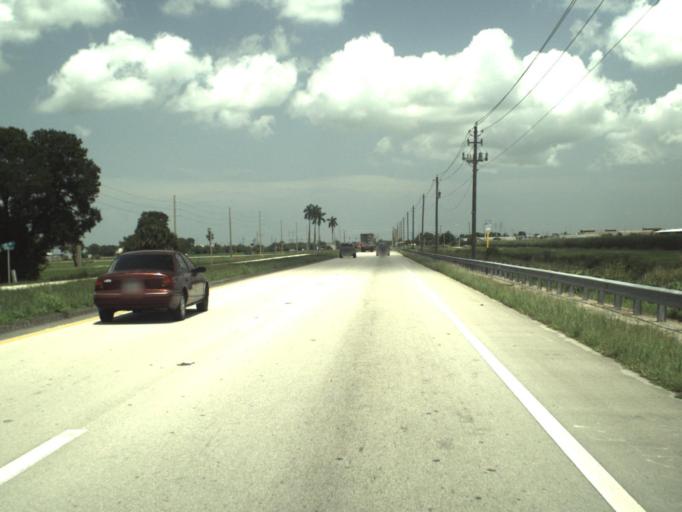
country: US
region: Florida
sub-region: Palm Beach County
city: Belle Glade
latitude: 26.7120
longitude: -80.6680
